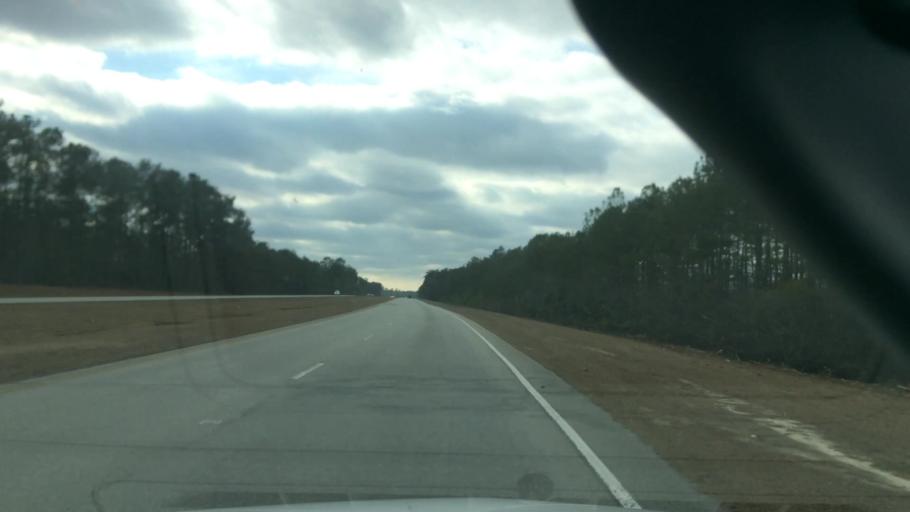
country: US
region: North Carolina
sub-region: Brunswick County
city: Bolivia
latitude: 34.0615
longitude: -78.2026
